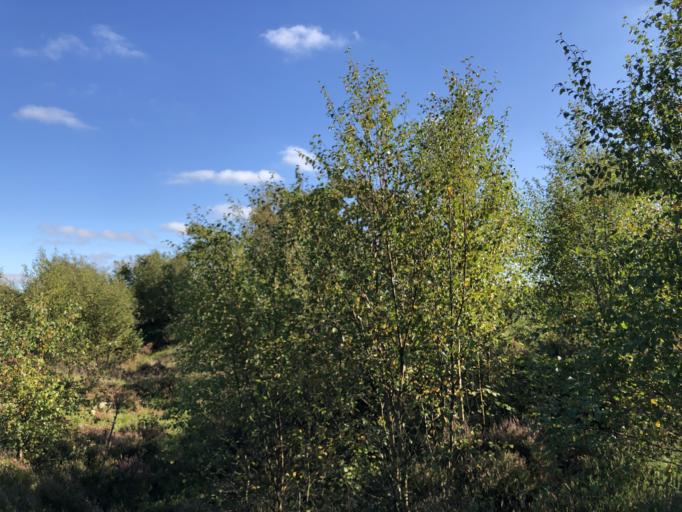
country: DK
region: Central Jutland
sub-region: Holstebro Kommune
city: Holstebro
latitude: 56.2477
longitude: 8.4921
